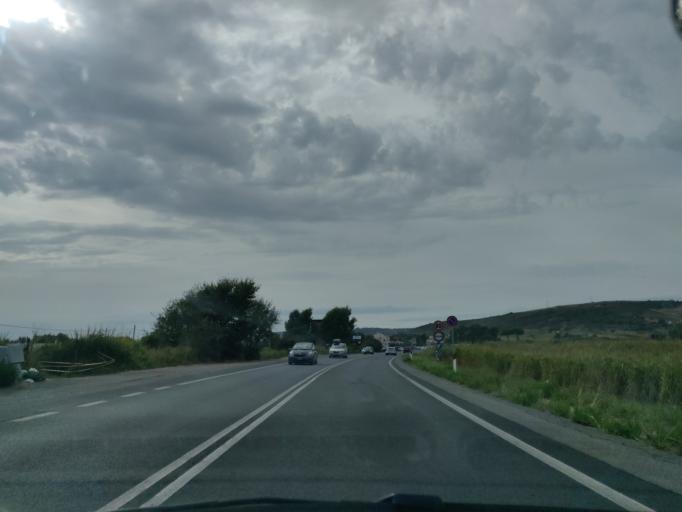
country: IT
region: Latium
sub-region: Citta metropolitana di Roma Capitale
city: Santa Marinella
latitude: 42.0365
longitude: 11.9238
